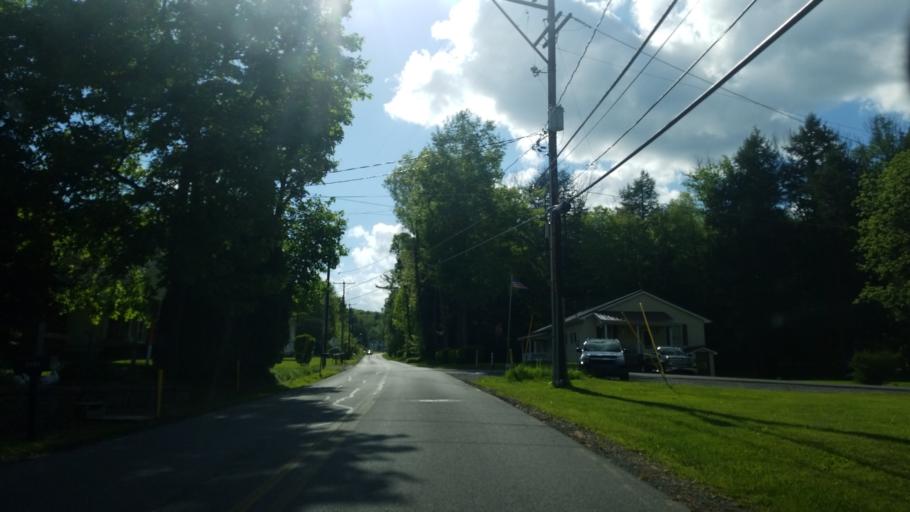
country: US
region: Pennsylvania
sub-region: Clearfield County
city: Troy
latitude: 40.9287
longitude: -78.2837
